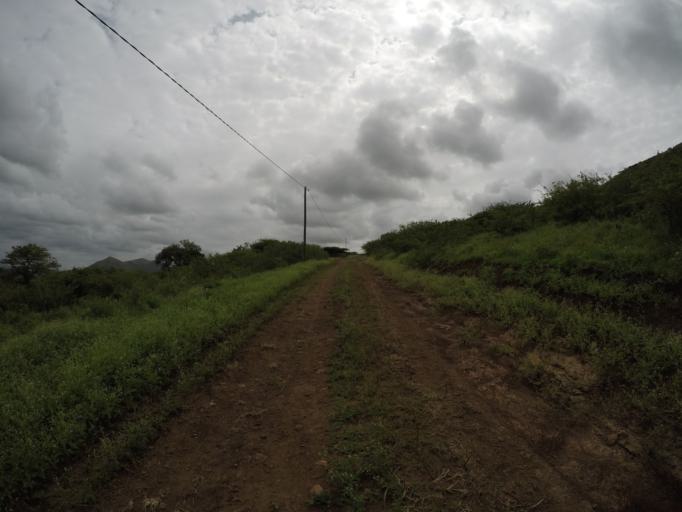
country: ZA
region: KwaZulu-Natal
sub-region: uThungulu District Municipality
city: Empangeni
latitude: -28.6179
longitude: 31.8863
